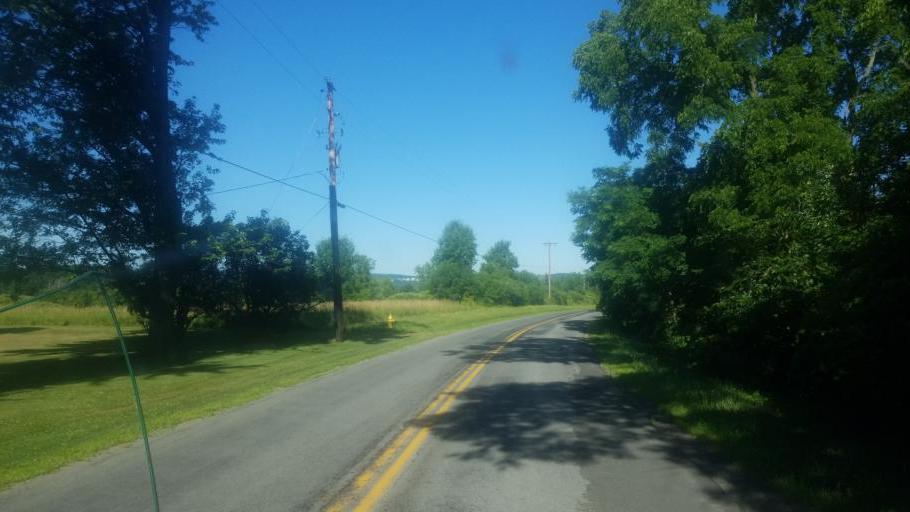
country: US
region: New York
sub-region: Ontario County
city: Canandaigua
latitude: 42.8390
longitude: -77.2410
